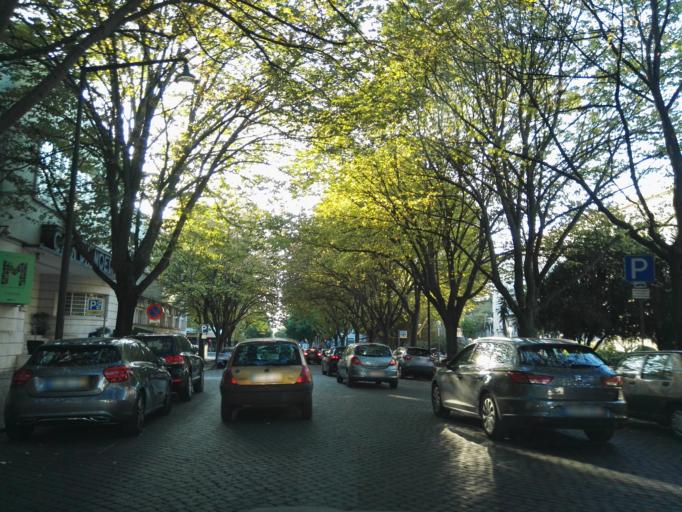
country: PT
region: Lisbon
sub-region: Lisbon
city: Lisbon
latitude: 38.7378
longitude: -9.1426
